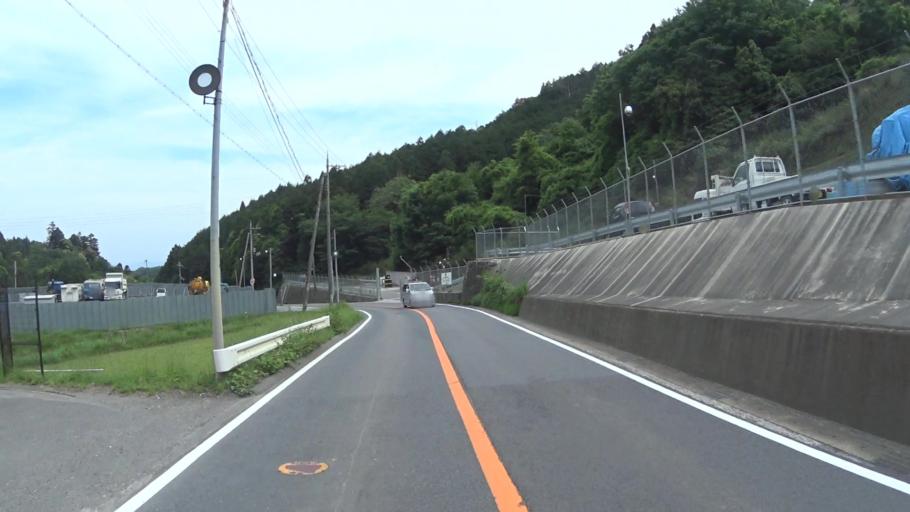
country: JP
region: Shiga Prefecture
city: Kitahama
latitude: 35.1631
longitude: 135.8620
